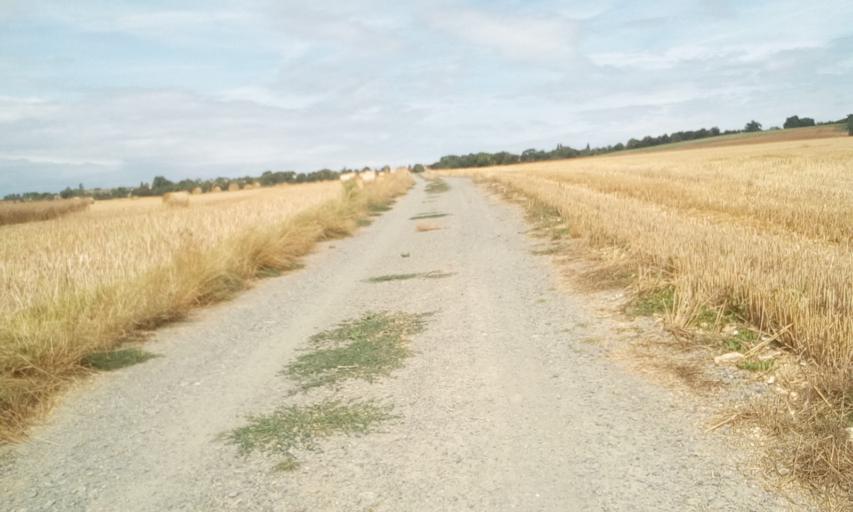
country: FR
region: Lower Normandy
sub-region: Departement du Calvados
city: Herouvillette
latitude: 49.2297
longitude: -0.2348
